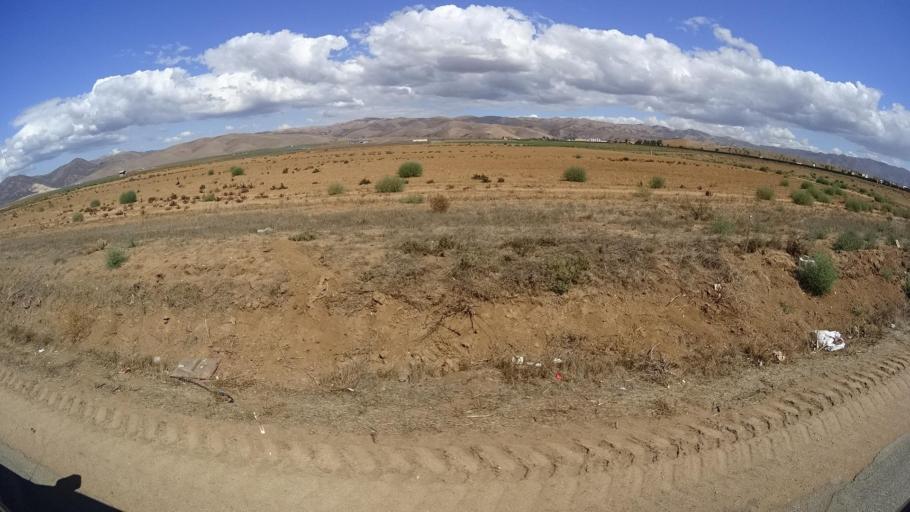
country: US
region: California
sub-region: Monterey County
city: Gonzales
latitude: 36.5299
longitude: -121.4215
